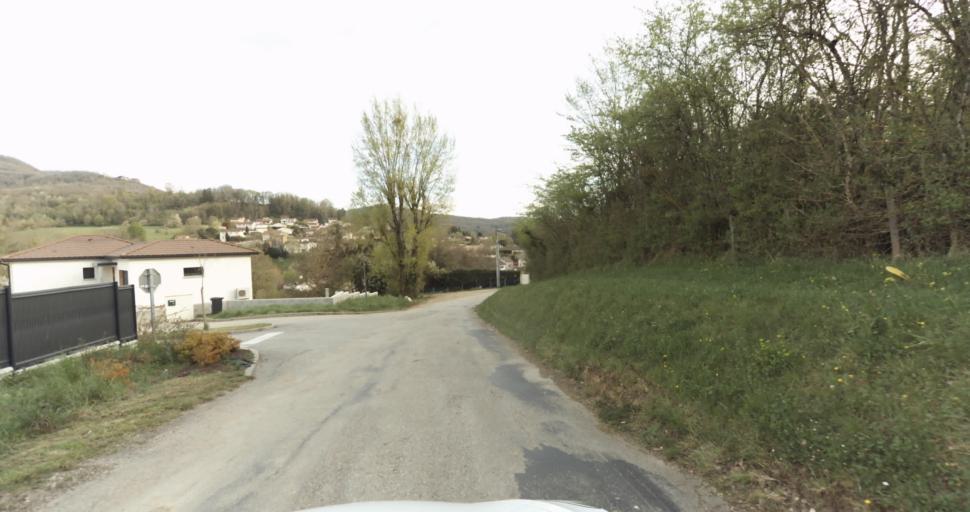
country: FR
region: Rhone-Alpes
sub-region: Departement de l'Ain
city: Amberieu-en-Bugey
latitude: 45.9583
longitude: 5.3650
